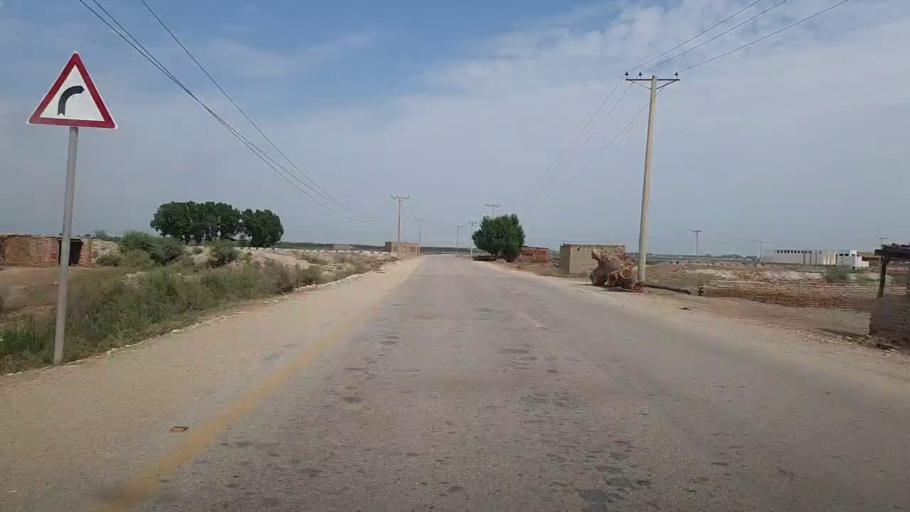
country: PK
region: Sindh
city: Thul
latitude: 28.2569
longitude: 68.7758
